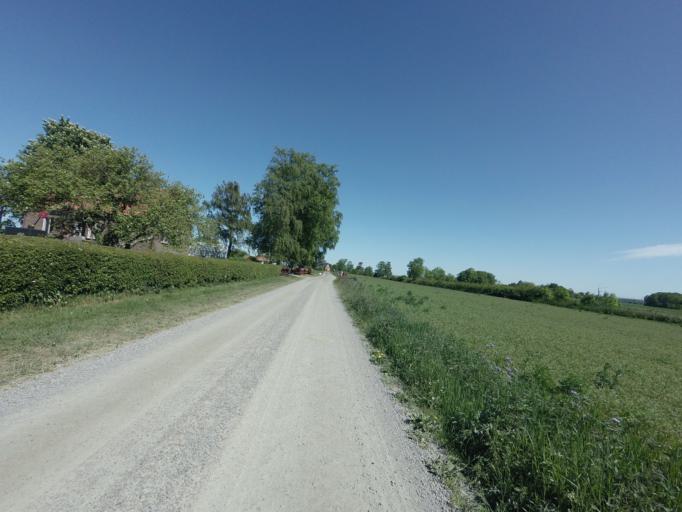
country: SE
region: Skane
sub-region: Helsingborg
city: Odakra
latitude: 56.1049
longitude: 12.7171
